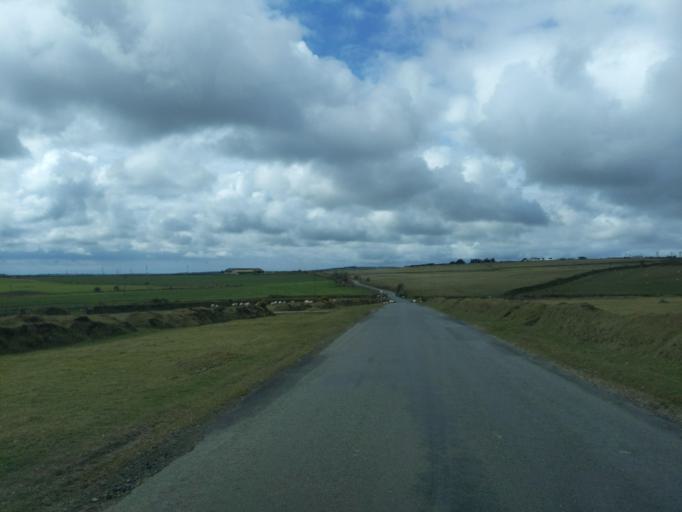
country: GB
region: England
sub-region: Cornwall
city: Camelford
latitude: 50.6398
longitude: -4.6307
